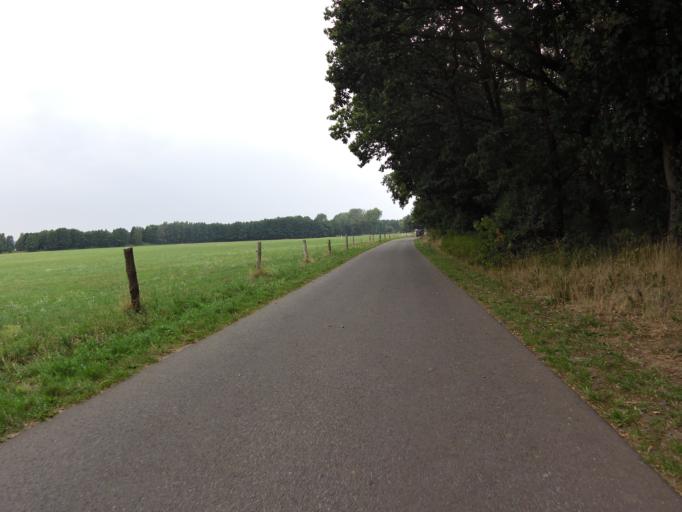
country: DE
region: Mecklenburg-Vorpommern
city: Seebad Heringsdorf
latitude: 53.9253
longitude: 14.1573
